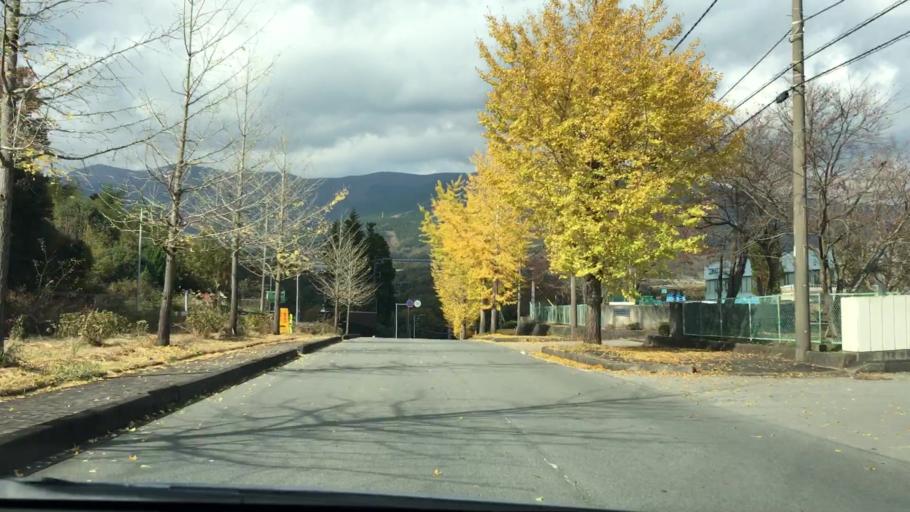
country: JP
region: Shizuoka
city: Gotemba
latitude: 35.3569
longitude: 138.9440
